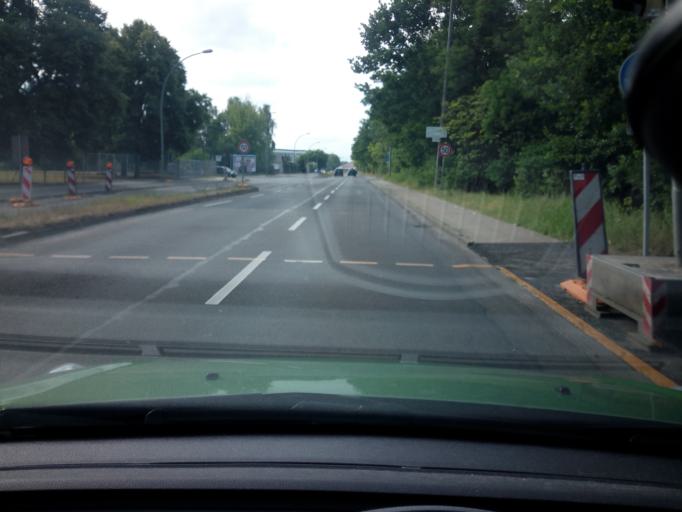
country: DE
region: Berlin
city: Oberschoneweide
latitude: 52.4745
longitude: 13.5083
